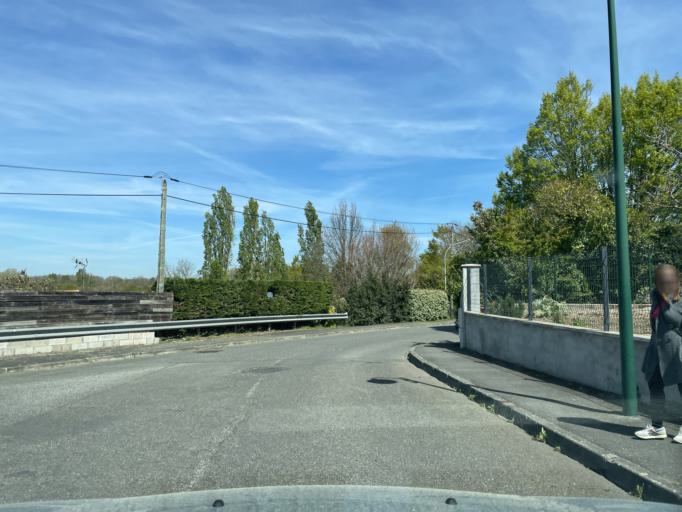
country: FR
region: Midi-Pyrenees
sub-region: Departement de la Haute-Garonne
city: Pibrac
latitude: 43.6174
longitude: 1.2695
